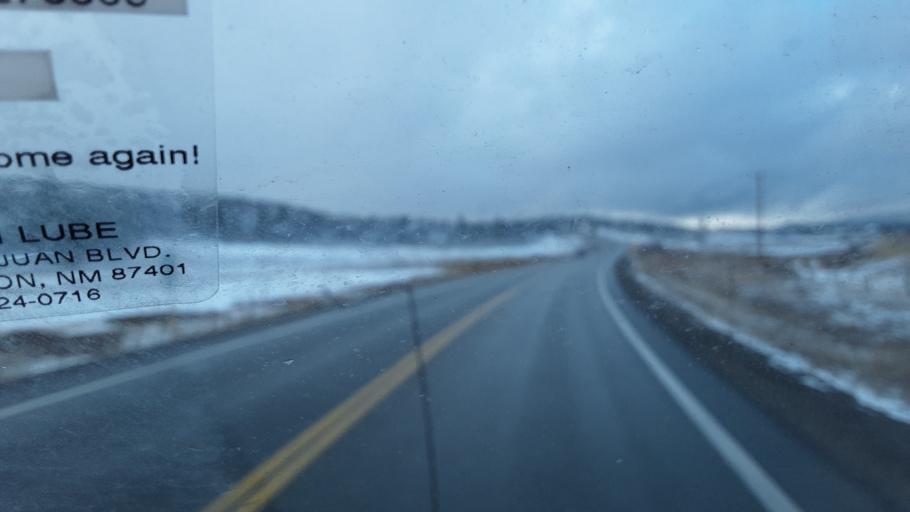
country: US
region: Colorado
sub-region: La Plata County
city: Bayfield
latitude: 37.2237
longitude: -107.6785
